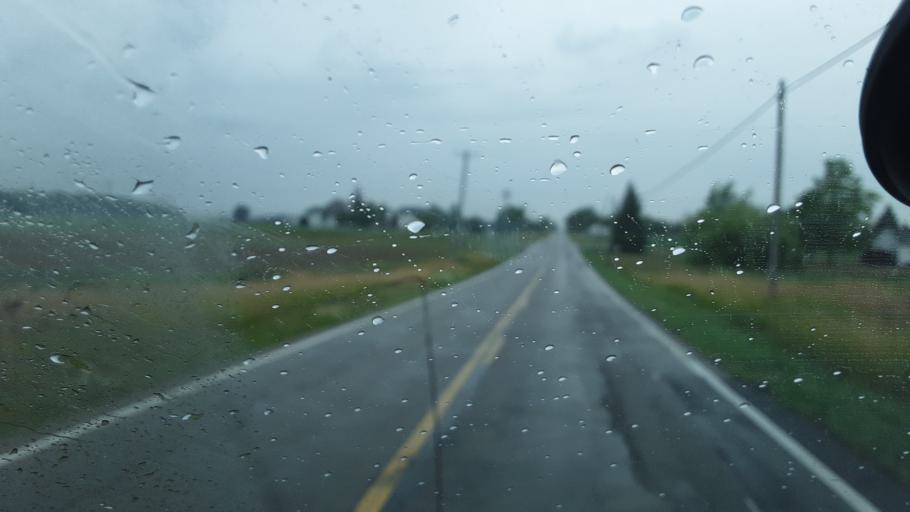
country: US
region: Ohio
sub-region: Williams County
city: Montpelier
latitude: 41.5269
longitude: -84.6129
